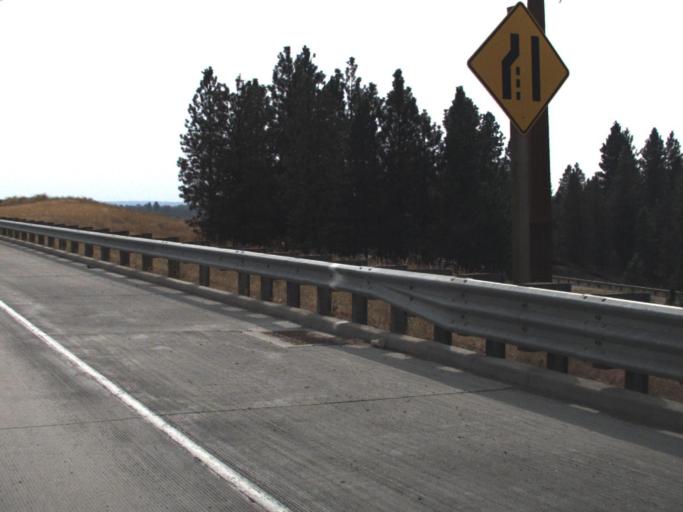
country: US
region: Washington
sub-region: Spokane County
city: Mead
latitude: 47.7423
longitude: -117.3607
